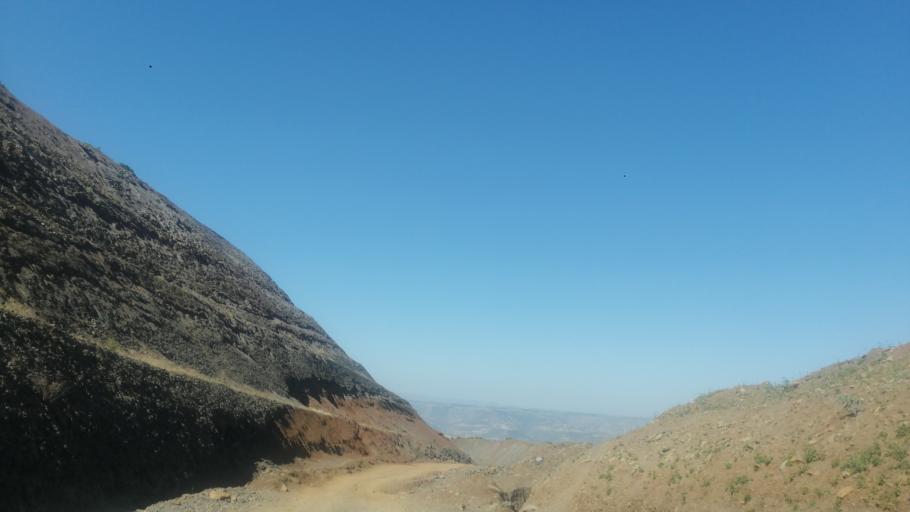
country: ET
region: Amhara
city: Addiet Canna
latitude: 11.1529
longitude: 37.8544
